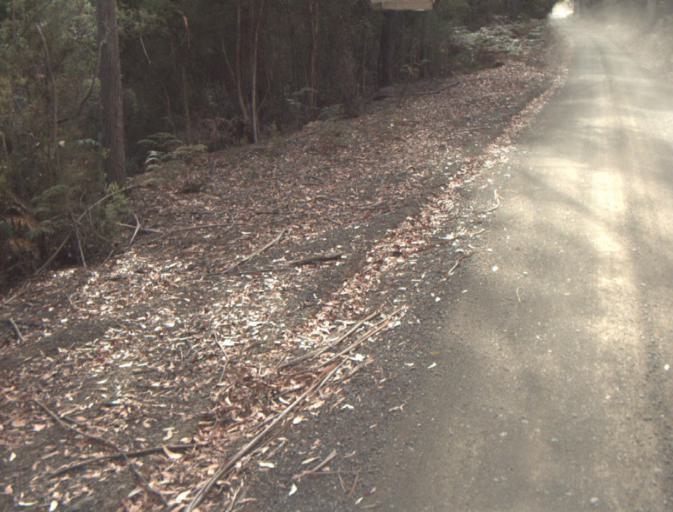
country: AU
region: Tasmania
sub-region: Launceston
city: Mayfield
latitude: -41.2652
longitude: 147.2368
